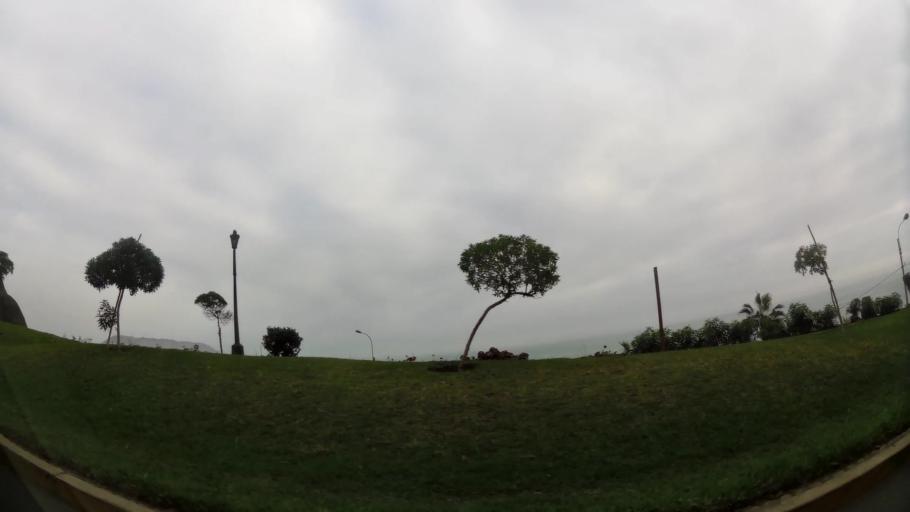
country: PE
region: Lima
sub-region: Lima
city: San Isidro
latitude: -12.1274
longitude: -77.0367
